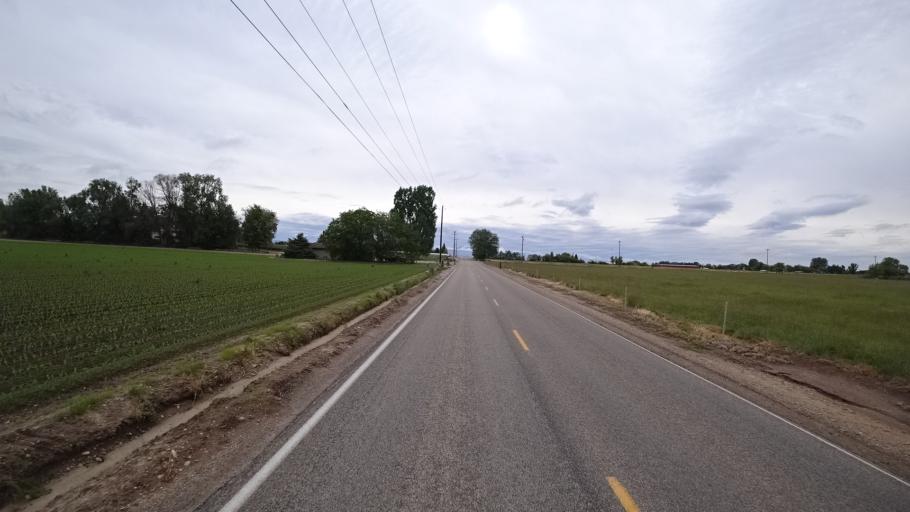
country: US
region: Idaho
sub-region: Ada County
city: Star
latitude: 43.7065
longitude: -116.4753
